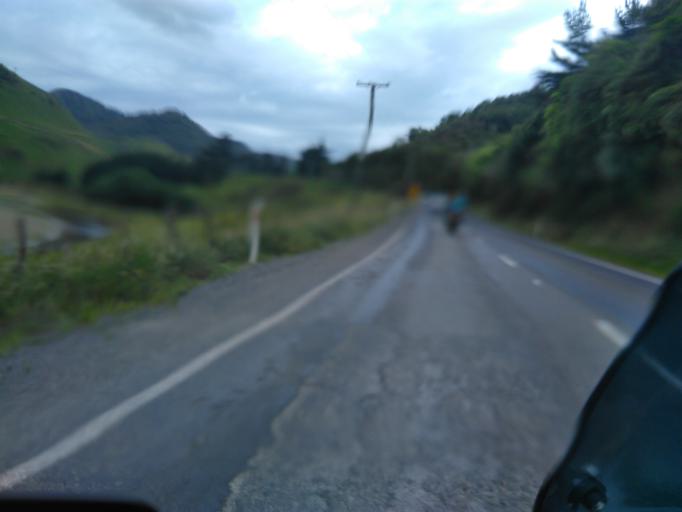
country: NZ
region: Bay of Plenty
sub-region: Opotiki District
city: Opotiki
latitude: -38.3728
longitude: 177.4875
